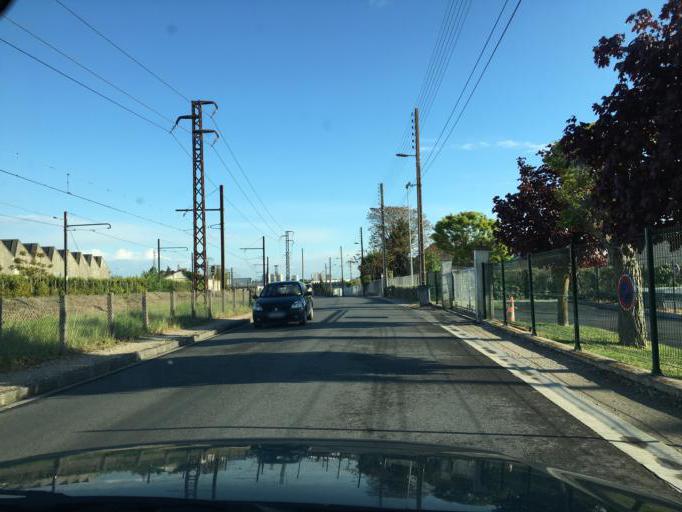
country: FR
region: Centre
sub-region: Departement du Loiret
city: Fleury-les-Aubrais
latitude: 47.9309
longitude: 1.8994
